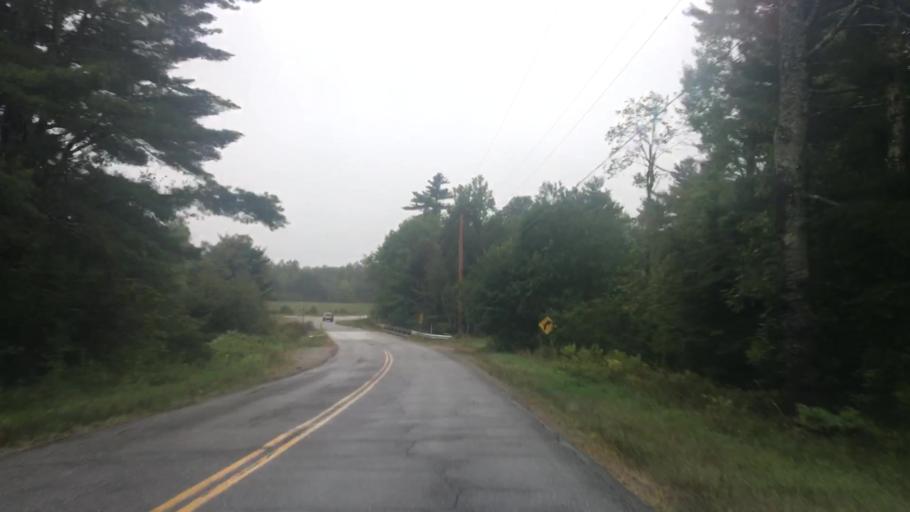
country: US
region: Maine
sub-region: Waldo County
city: Frankfort
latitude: 44.5501
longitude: -68.8724
